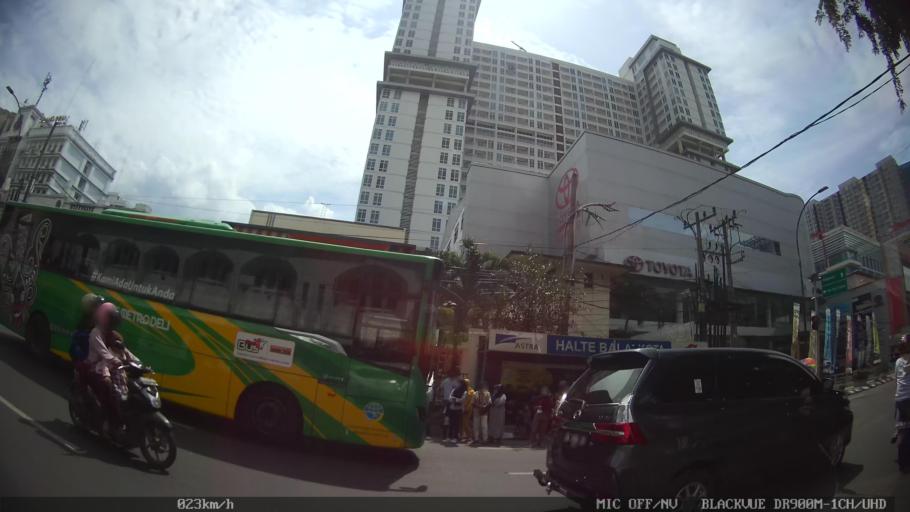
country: ID
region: North Sumatra
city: Medan
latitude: 3.5919
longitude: 98.6771
